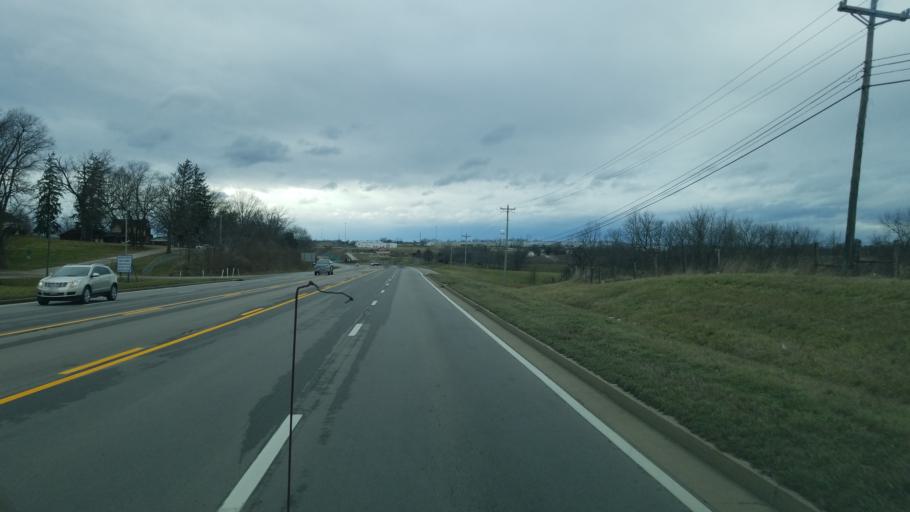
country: US
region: Ohio
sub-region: Brown County
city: Aberdeen
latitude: 38.6410
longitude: -83.8176
